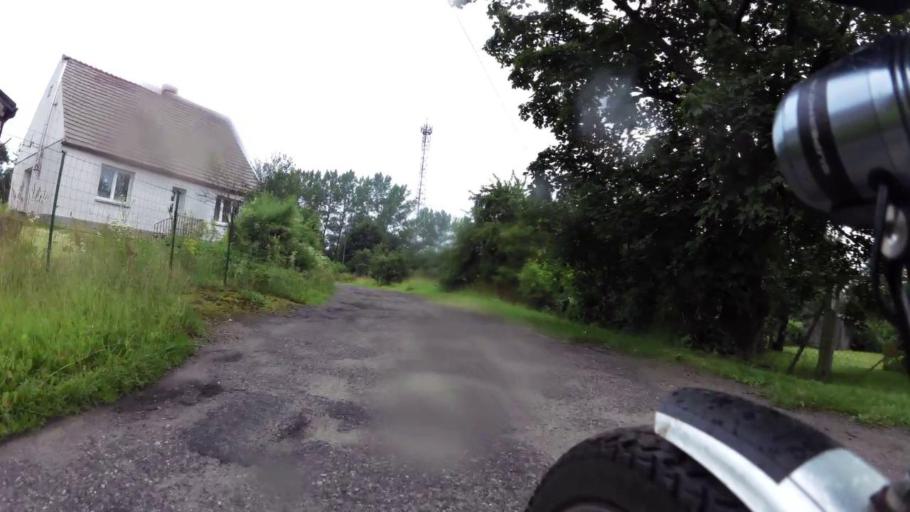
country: PL
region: West Pomeranian Voivodeship
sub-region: Powiat lobeski
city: Lobez
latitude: 53.7031
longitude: 15.6062
